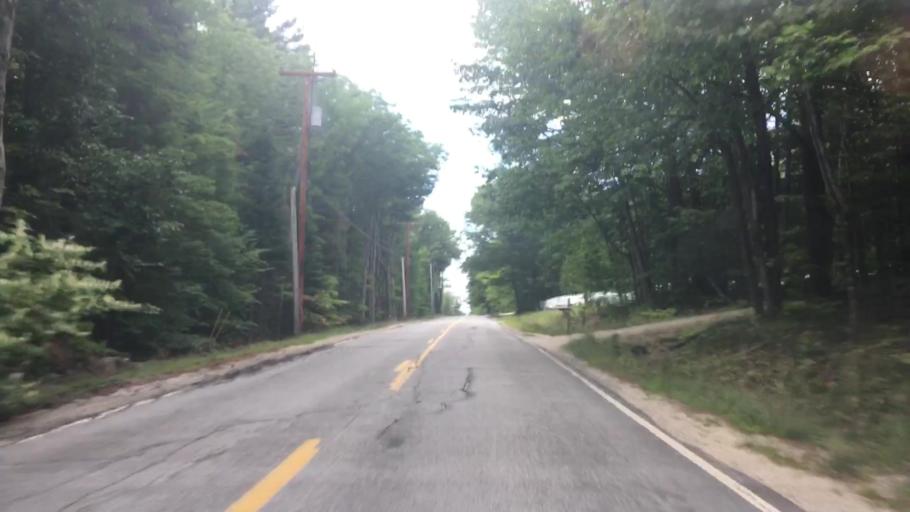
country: US
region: Maine
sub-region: Oxford County
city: Oxford
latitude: 44.0438
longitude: -70.5434
